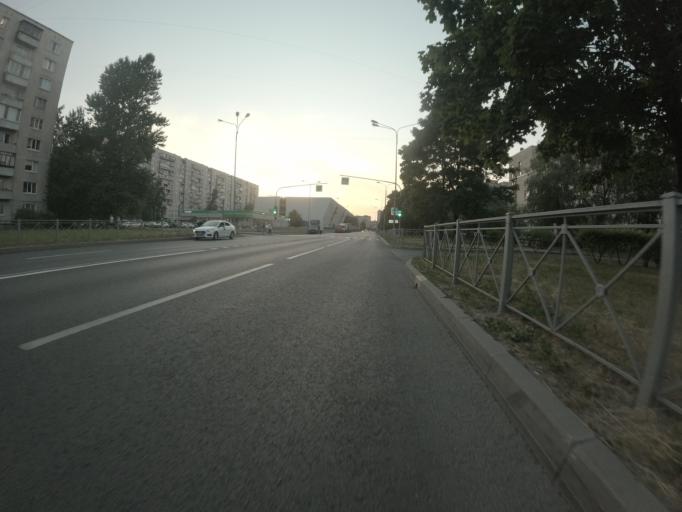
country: RU
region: St.-Petersburg
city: Krasnogvargeisky
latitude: 59.9116
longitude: 30.4614
